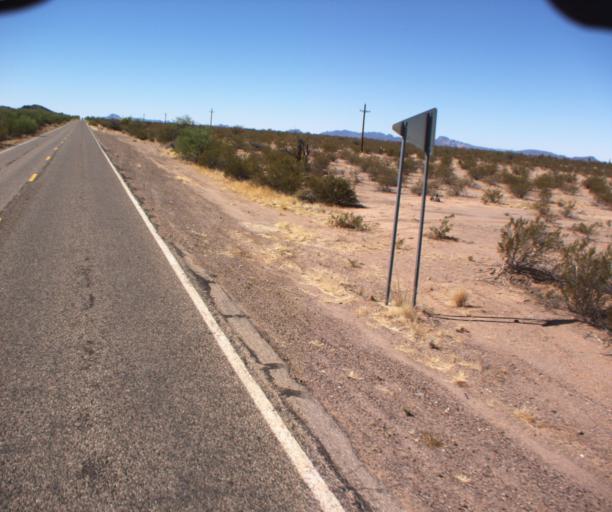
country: US
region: Arizona
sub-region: Pima County
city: Ajo
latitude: 32.2558
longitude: -112.7436
